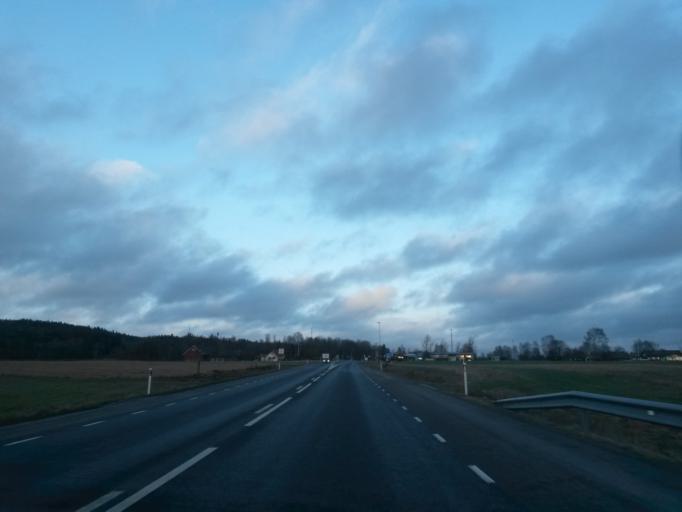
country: SE
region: Halland
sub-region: Halmstads Kommun
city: Aled
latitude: 56.7436
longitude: 12.9288
